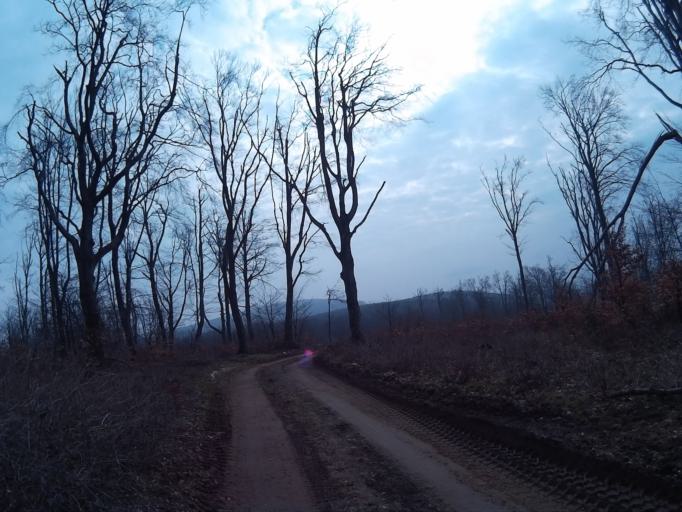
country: HU
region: Veszprem
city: Zirc
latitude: 47.1872
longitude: 17.8332
